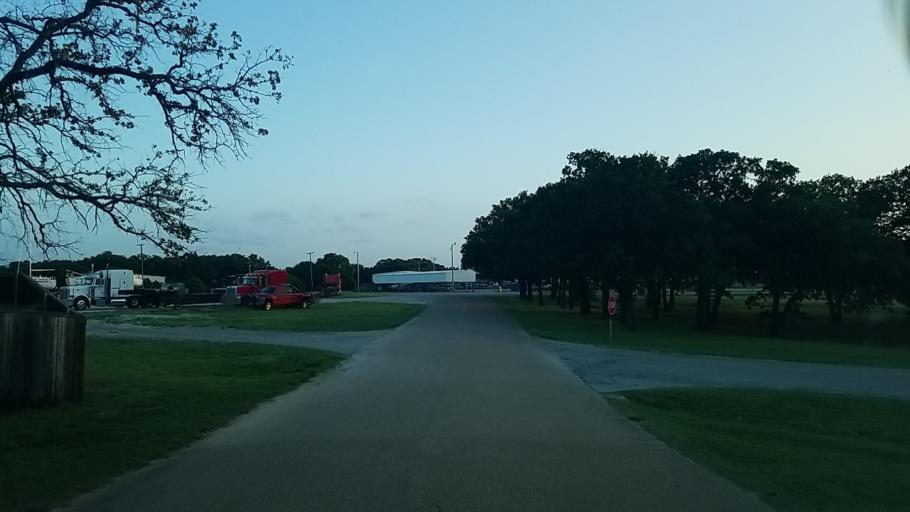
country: US
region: Texas
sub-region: Denton County
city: Highland Village
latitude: 33.0834
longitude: -97.0215
